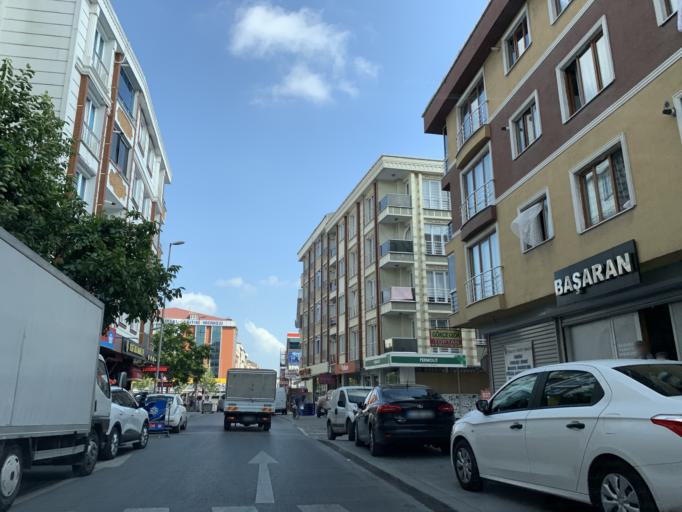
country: TR
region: Istanbul
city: Esenyurt
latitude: 41.0331
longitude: 28.6747
